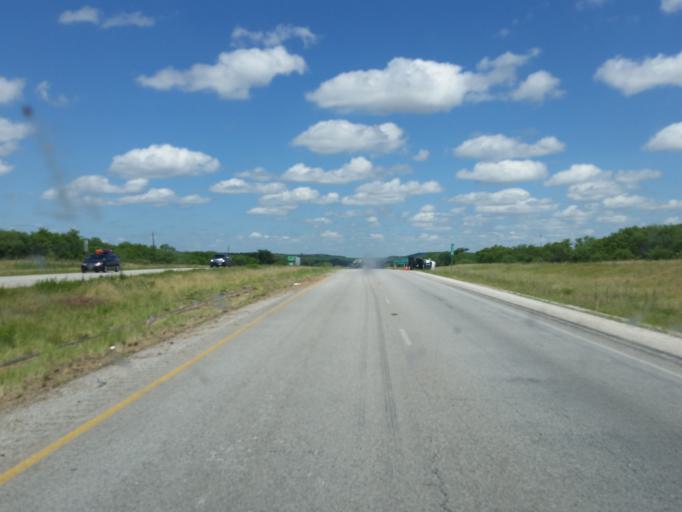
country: US
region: Texas
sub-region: Callahan County
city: Baird
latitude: 32.3803
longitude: -99.2673
